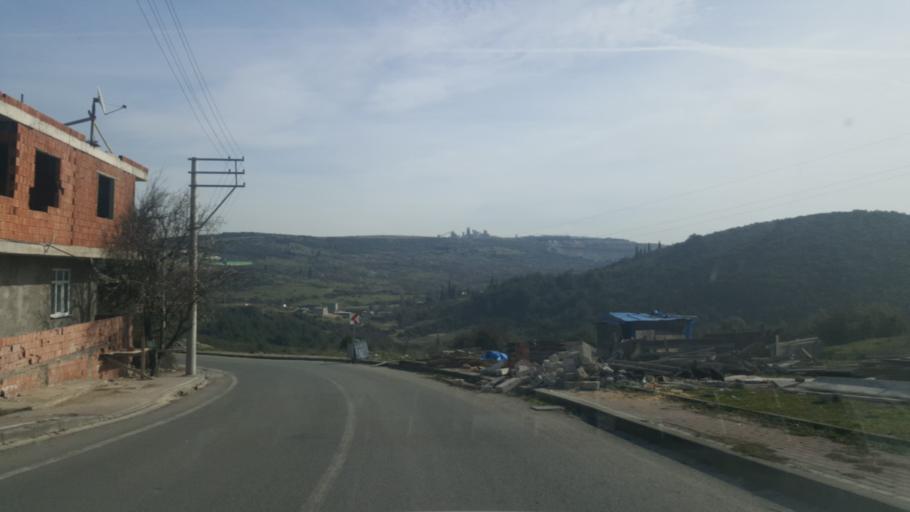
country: TR
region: Kocaeli
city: Tavsancil
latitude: 40.7852
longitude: 29.5595
